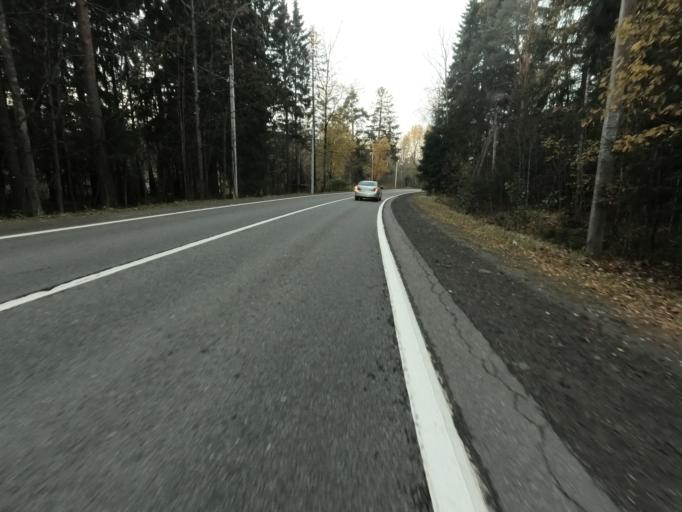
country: RU
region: St.-Petersburg
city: Repino
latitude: 60.1932
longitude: 29.8557
